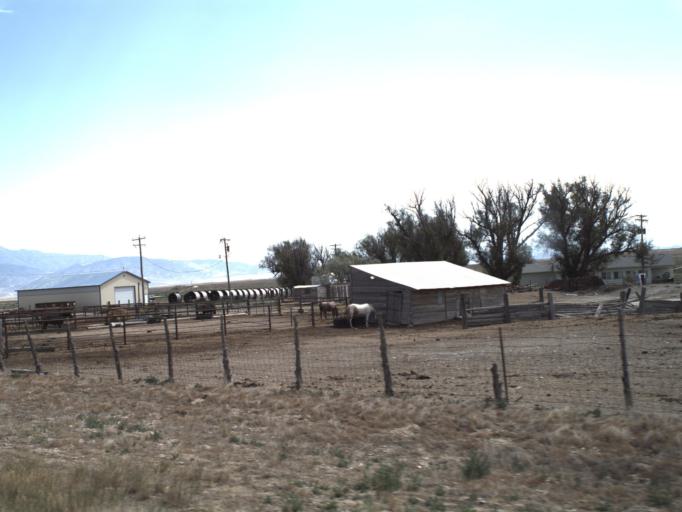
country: US
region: Utah
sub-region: Tooele County
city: Tooele
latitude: 40.1707
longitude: -112.4287
